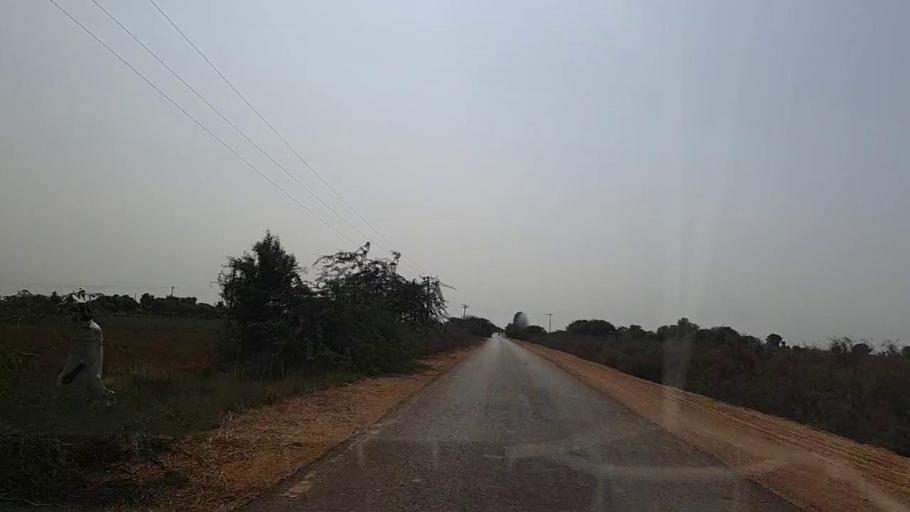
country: PK
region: Sindh
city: Chuhar Jamali
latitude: 24.3194
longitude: 67.9407
